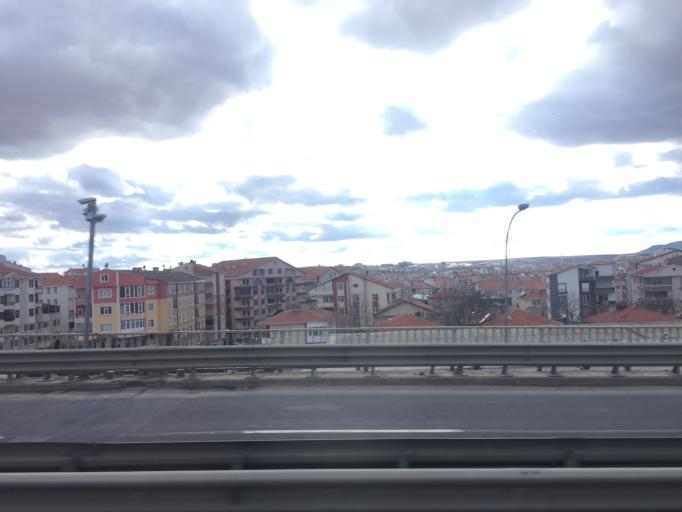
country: TR
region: Kirsehir
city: Kirsehir
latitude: 39.1597
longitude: 34.1606
